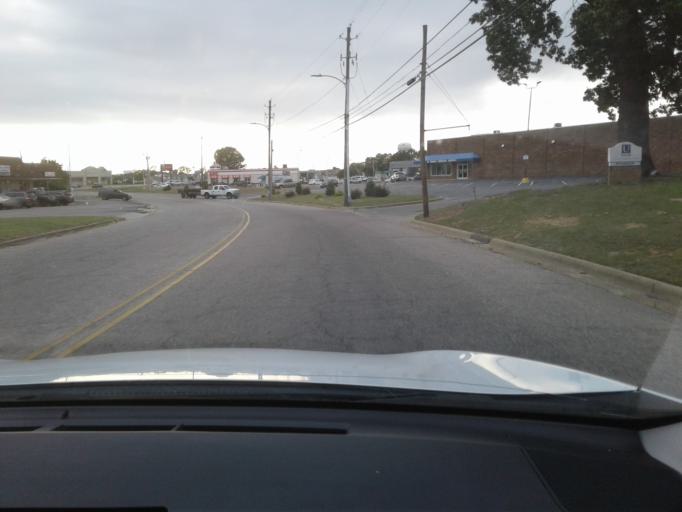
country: US
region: North Carolina
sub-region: Harnett County
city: Dunn
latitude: 35.3154
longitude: -78.6228
